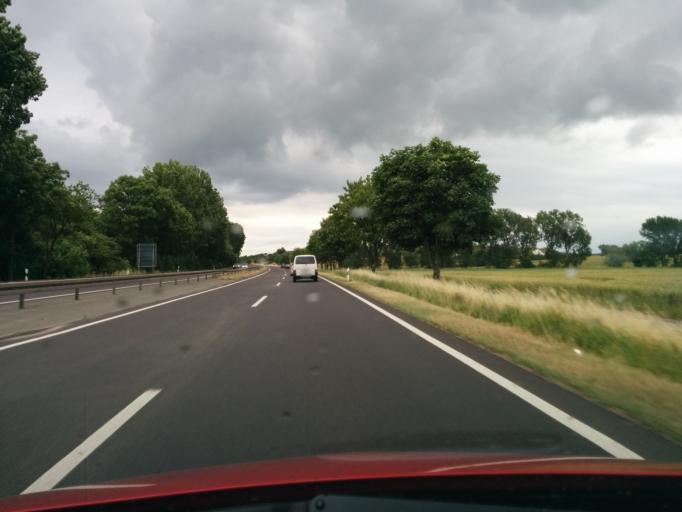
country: DE
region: Thuringia
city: Elxleben
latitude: 51.0409
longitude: 10.9442
